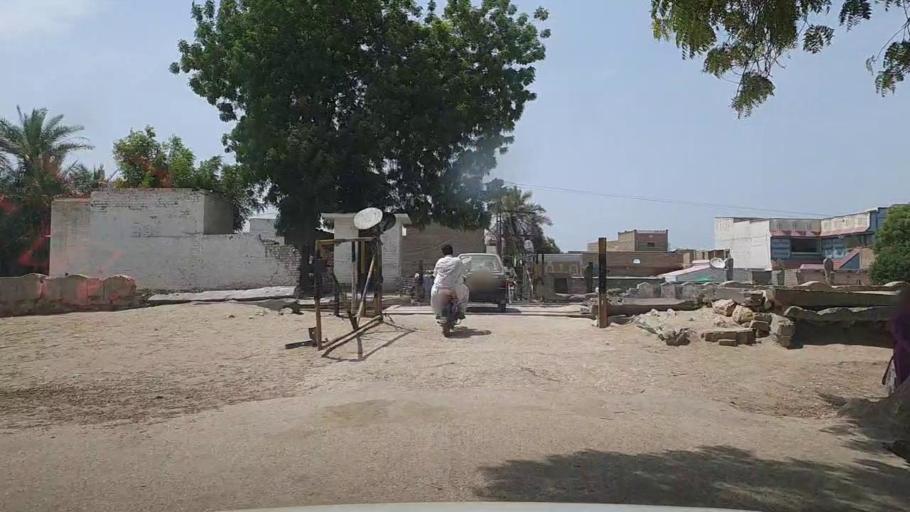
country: PK
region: Sindh
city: Pano Aqil
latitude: 27.8548
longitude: 69.1188
